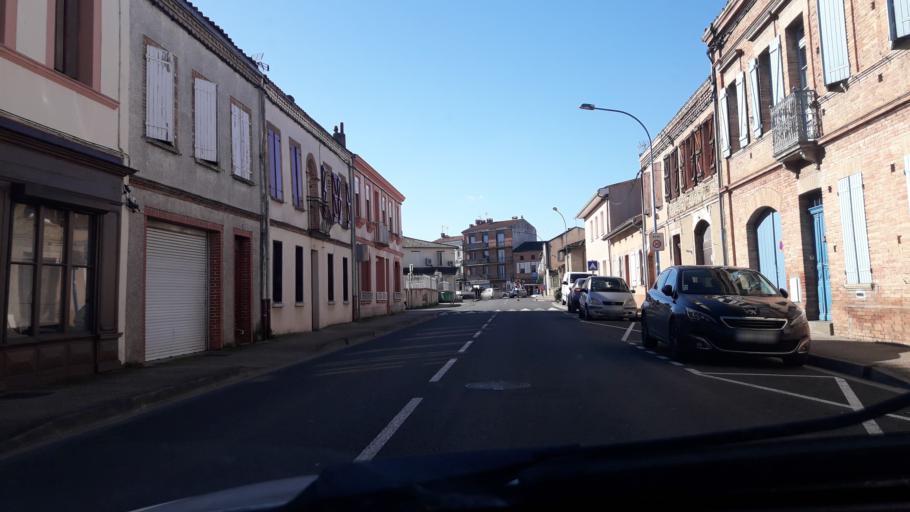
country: FR
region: Midi-Pyrenees
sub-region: Departement du Gers
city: Pujaudran
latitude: 43.6146
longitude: 1.0849
